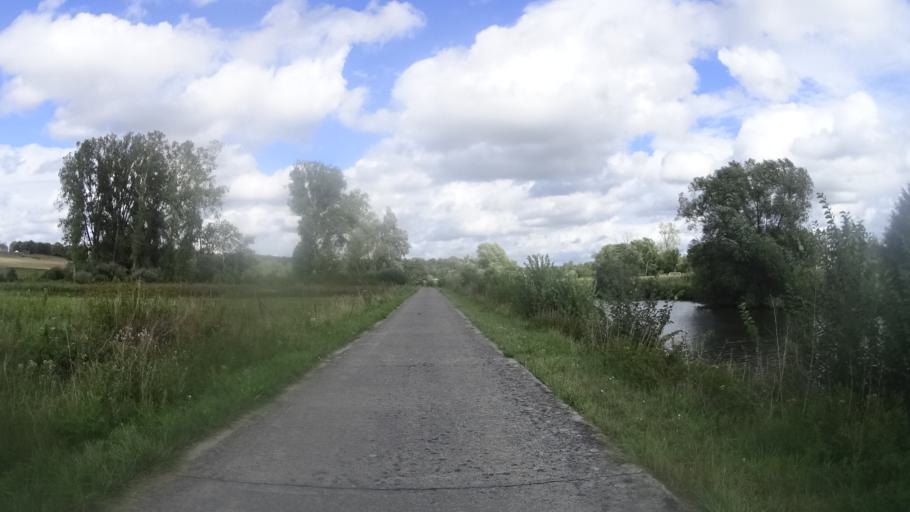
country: BE
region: Wallonia
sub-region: Province du Hainaut
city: Merbes-le-Chateau
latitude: 50.3229
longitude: 4.2076
